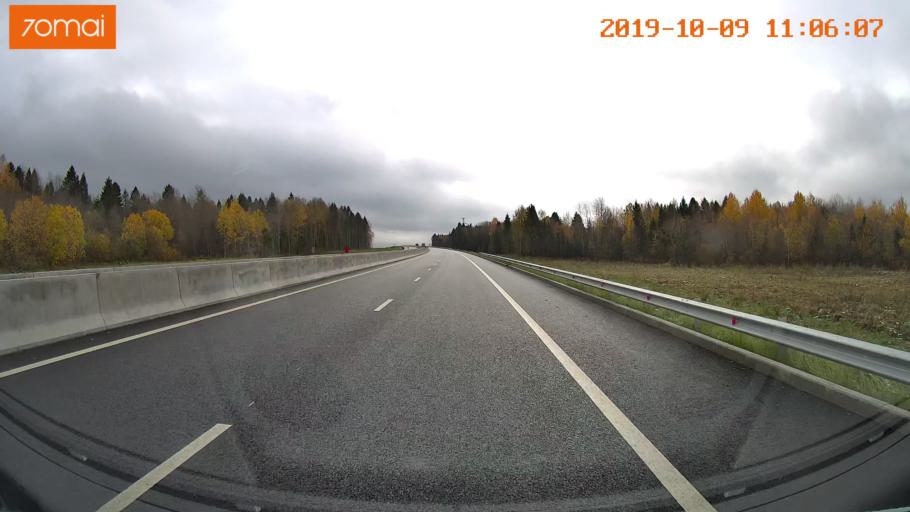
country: RU
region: Vologda
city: Molochnoye
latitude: 59.1907
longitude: 39.7585
